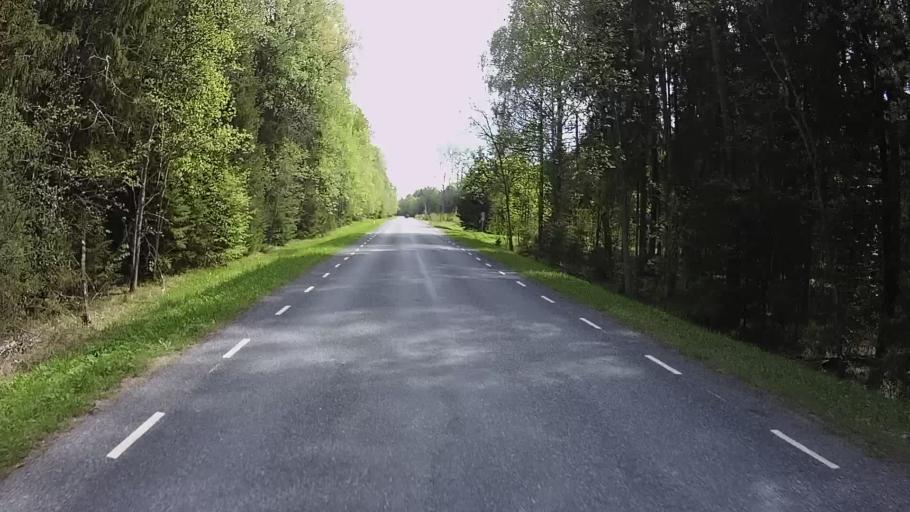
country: EE
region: Valgamaa
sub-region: Valga linn
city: Valga
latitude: 57.7017
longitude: 26.2444
